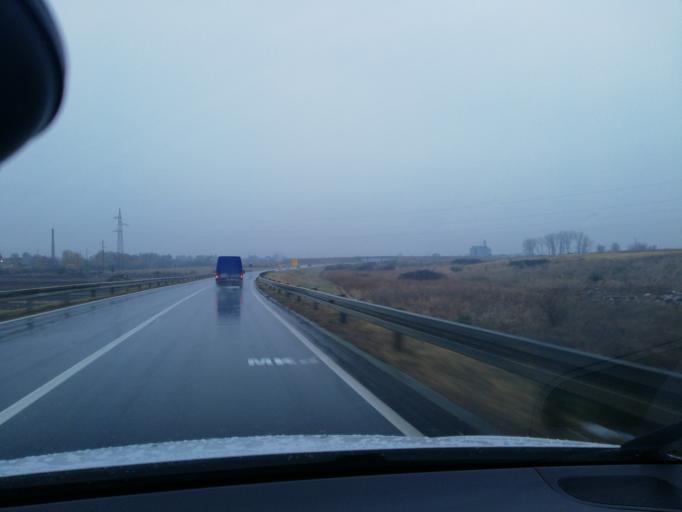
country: RS
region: Autonomna Pokrajina Vojvodina
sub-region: Sremski Okrug
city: Ruma
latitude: 45.0133
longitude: 19.8459
